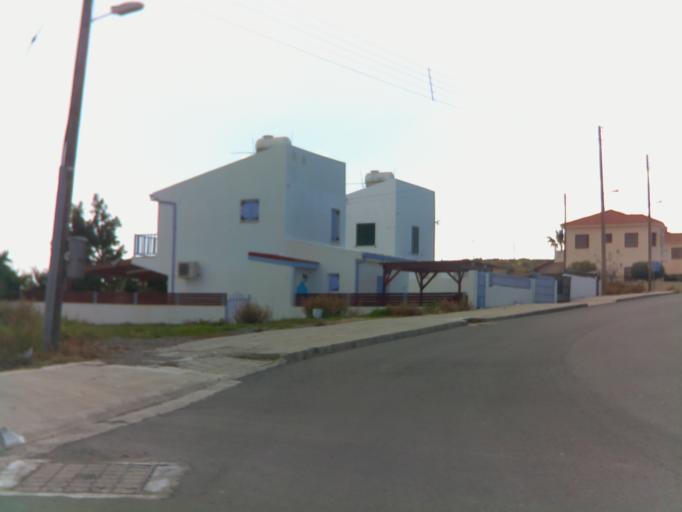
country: CY
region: Limassol
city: Pissouri
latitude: 34.6611
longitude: 32.6979
